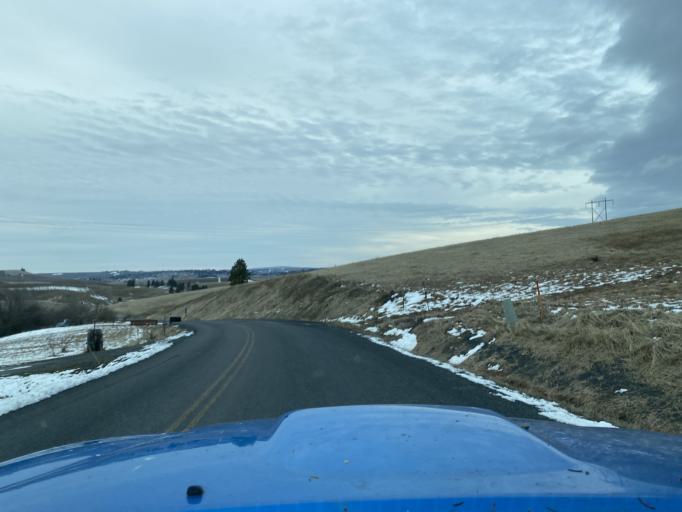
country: US
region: Idaho
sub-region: Latah County
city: Moscow
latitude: 46.7030
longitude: -116.9366
